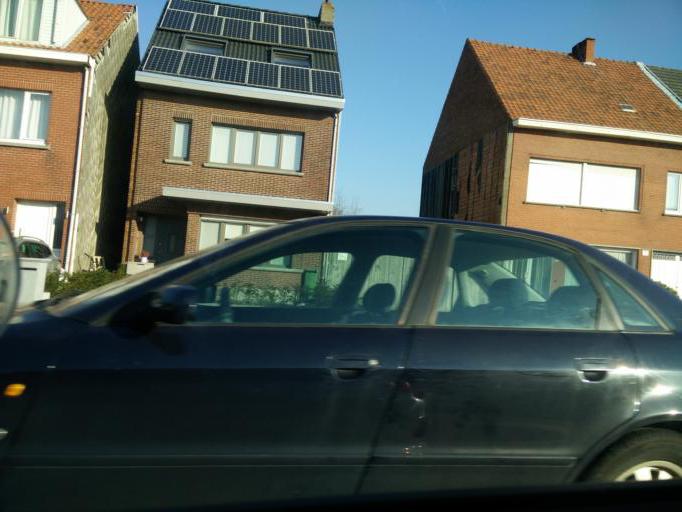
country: BE
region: Flanders
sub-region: Provincie Antwerpen
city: Kapellen
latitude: 51.2997
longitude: 4.4111
